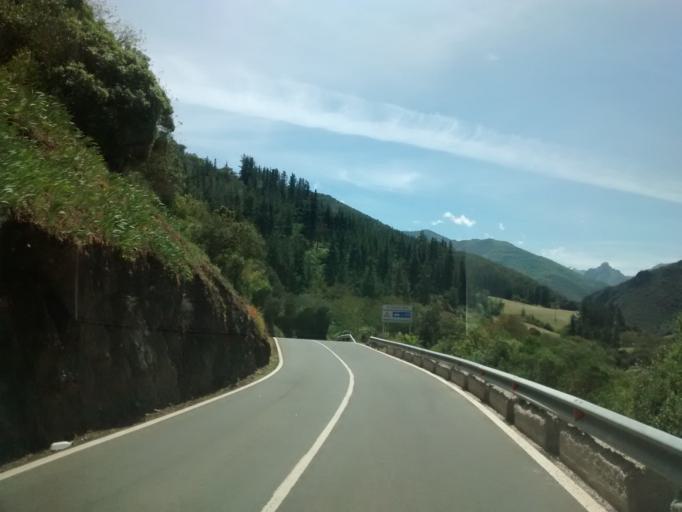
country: ES
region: Cantabria
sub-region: Provincia de Cantabria
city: Potes
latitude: 43.1429
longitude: -4.6278
